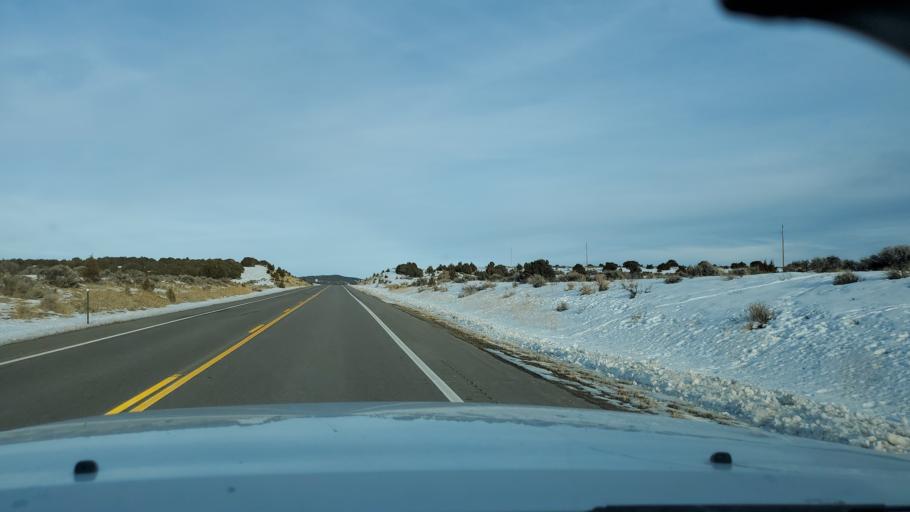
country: US
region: Colorado
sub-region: Rio Blanco County
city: Rangely
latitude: 40.3355
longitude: -108.4790
